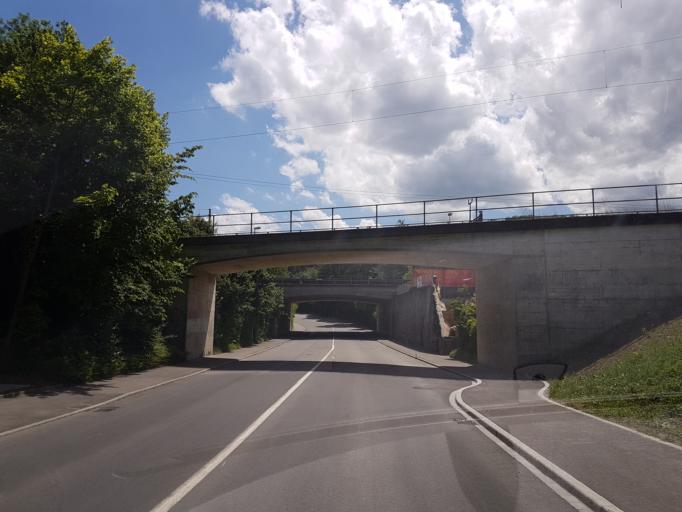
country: CH
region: Aargau
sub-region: Bezirk Lenzburg
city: Othmarsingen
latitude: 47.4147
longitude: 8.2330
